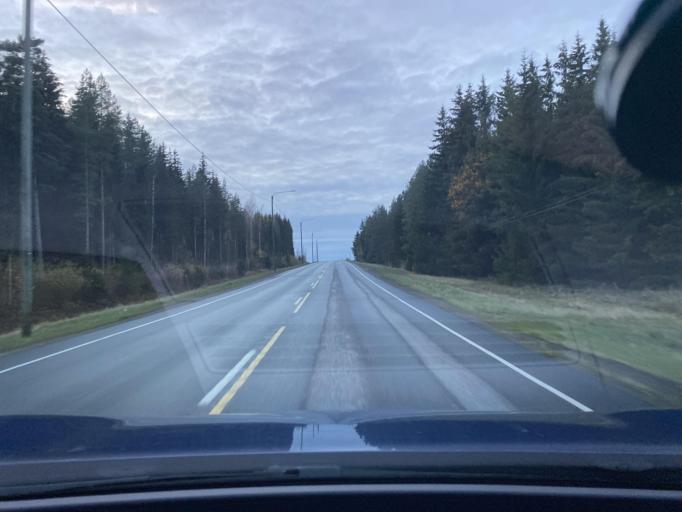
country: FI
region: Uusimaa
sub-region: Helsinki
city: Saukkola
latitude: 60.3870
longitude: 24.0557
